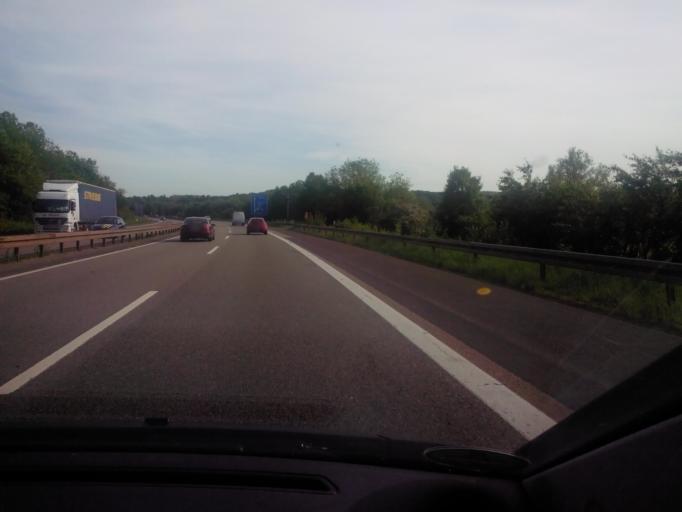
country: DE
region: Saarland
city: Saarlouis
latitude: 49.3124
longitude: 6.7298
